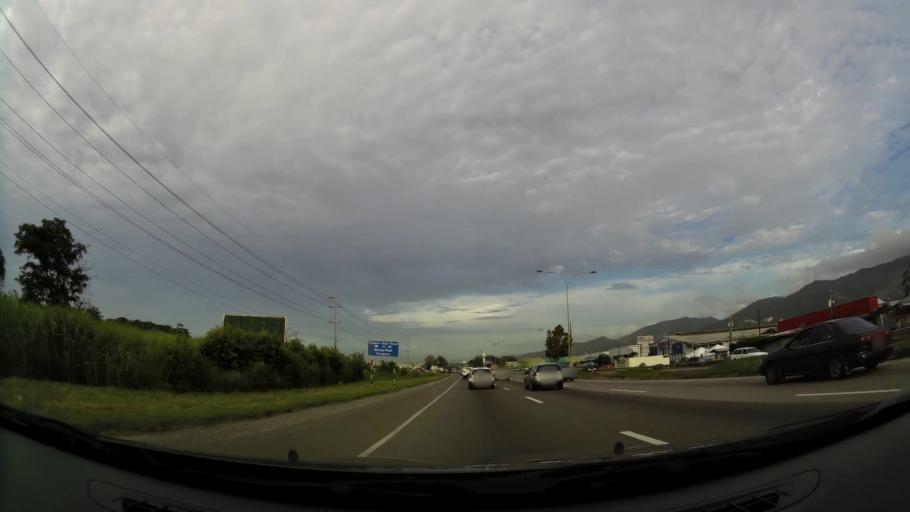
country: TT
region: Tunapuna/Piarco
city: Tunapuna
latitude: 10.6379
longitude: -61.3793
